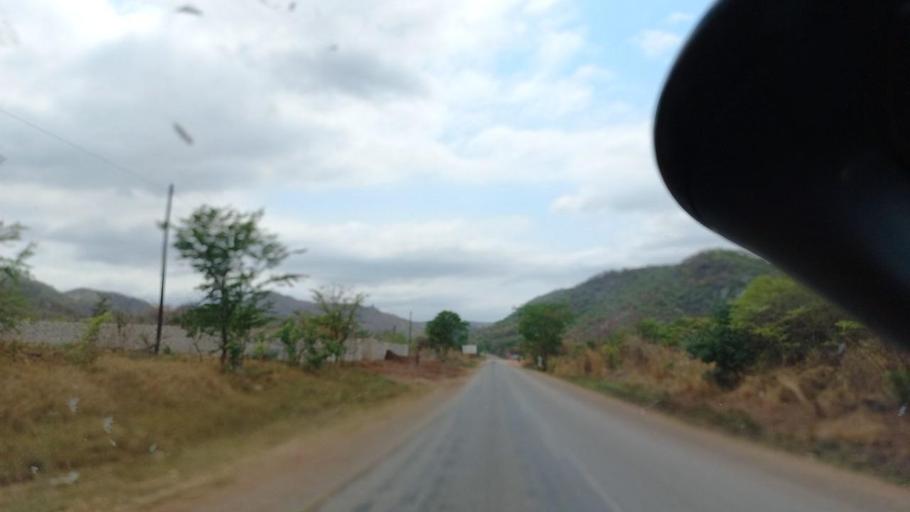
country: ZM
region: Lusaka
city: Luangwa
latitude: -15.0595
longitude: 29.7251
